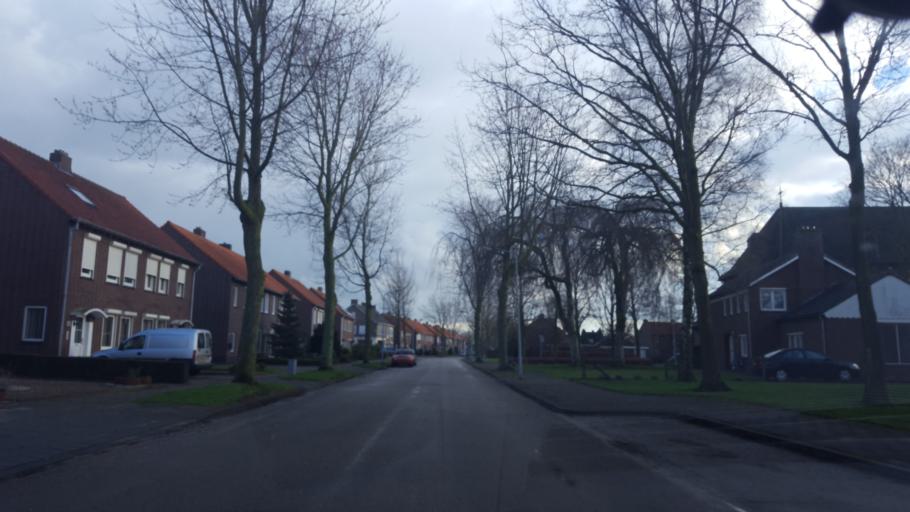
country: NL
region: Limburg
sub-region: Gemeente Weert
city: Weert
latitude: 51.2522
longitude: 5.7362
